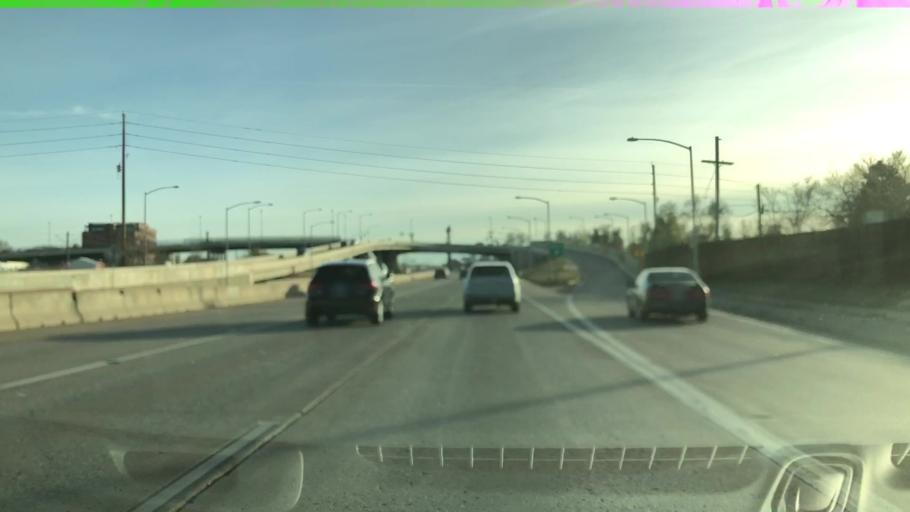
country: US
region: Colorado
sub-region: Arapahoe County
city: Englewood
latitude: 39.6811
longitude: -104.9927
